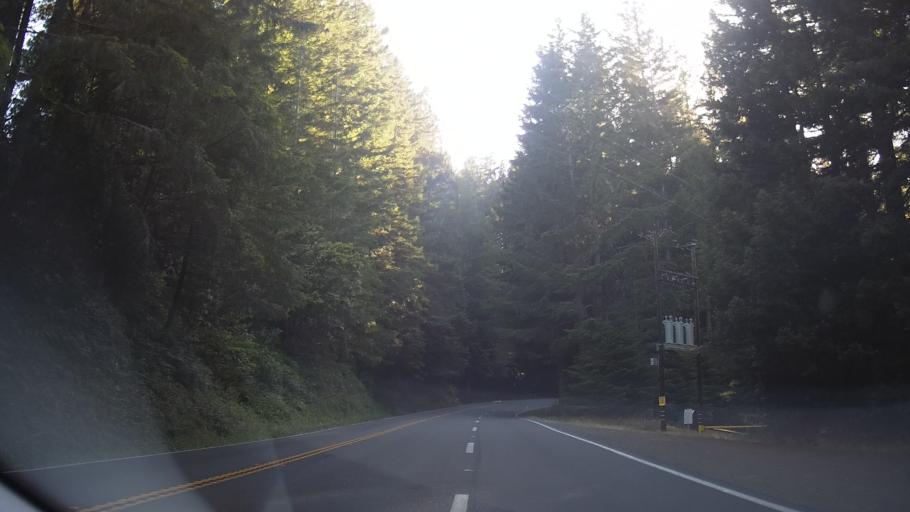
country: US
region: California
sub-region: Mendocino County
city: Fort Bragg
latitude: 39.3652
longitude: -123.6743
